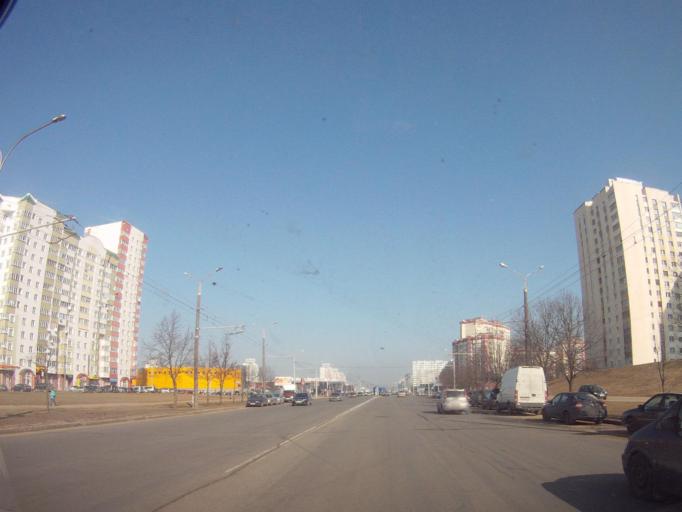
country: BY
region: Minsk
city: Novoye Medvezhino
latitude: 53.9033
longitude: 27.4355
